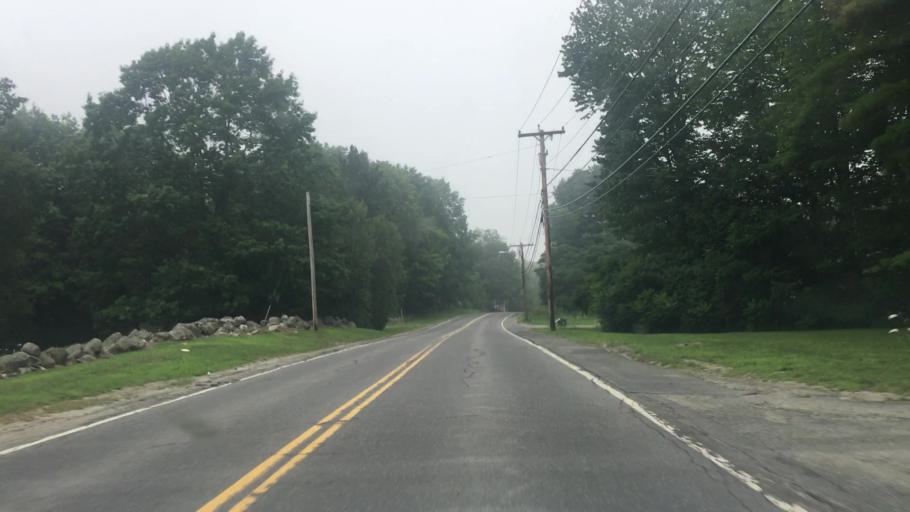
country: US
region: Maine
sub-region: Kennebec County
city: Oakland
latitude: 44.5347
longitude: -69.7231
